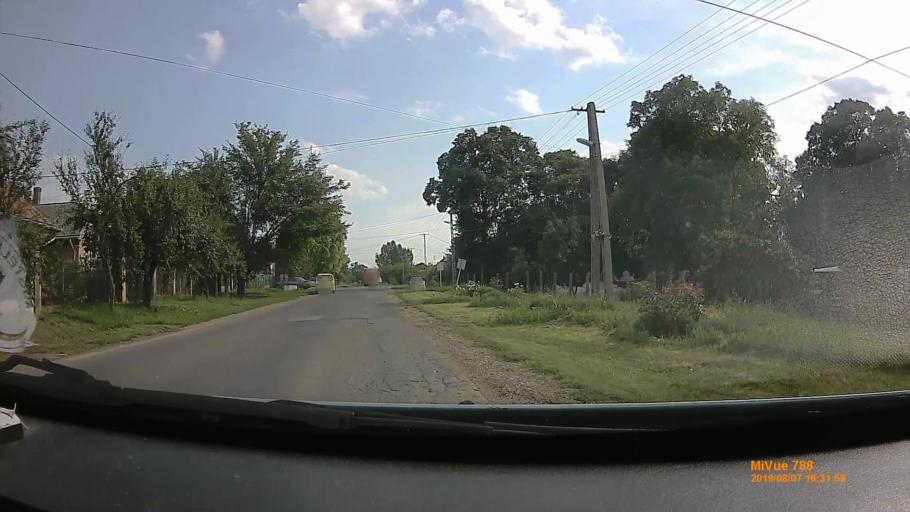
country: HU
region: Borsod-Abauj-Zemplen
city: Gonc
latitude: 48.4444
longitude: 21.2389
